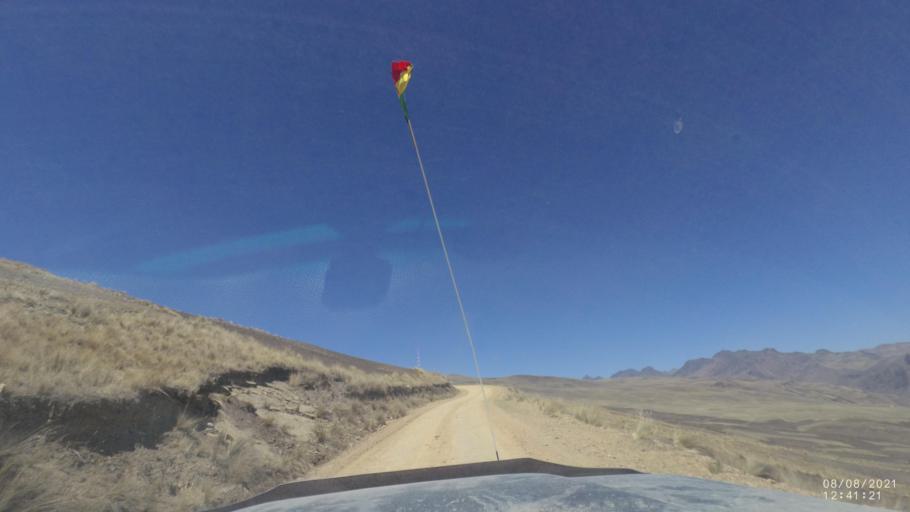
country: BO
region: Cochabamba
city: Colchani
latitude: -16.8338
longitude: -66.6201
